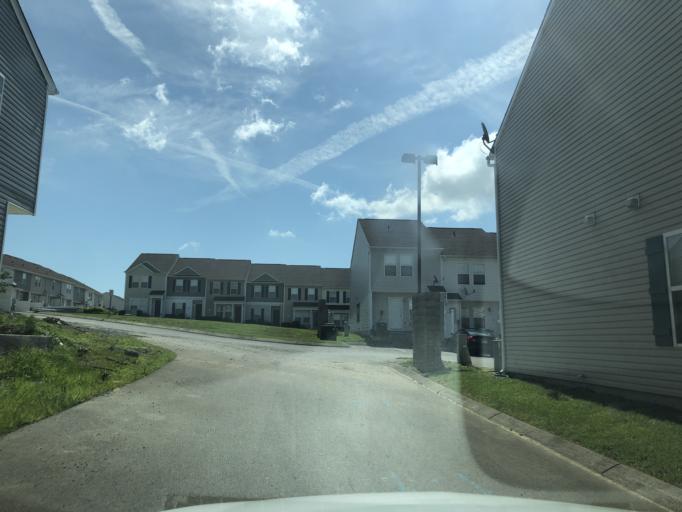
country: US
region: Tennessee
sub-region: Rutherford County
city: La Vergne
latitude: 36.0394
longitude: -86.6290
